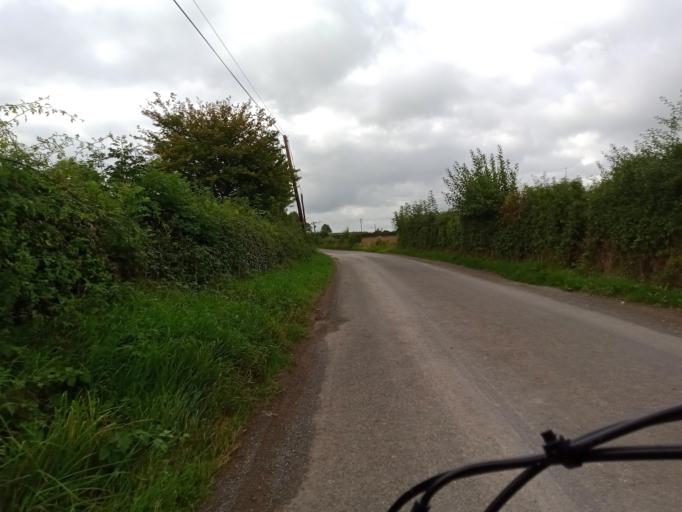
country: IE
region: Leinster
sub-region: Kilkenny
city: Callan
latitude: 52.5347
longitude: -7.2800
